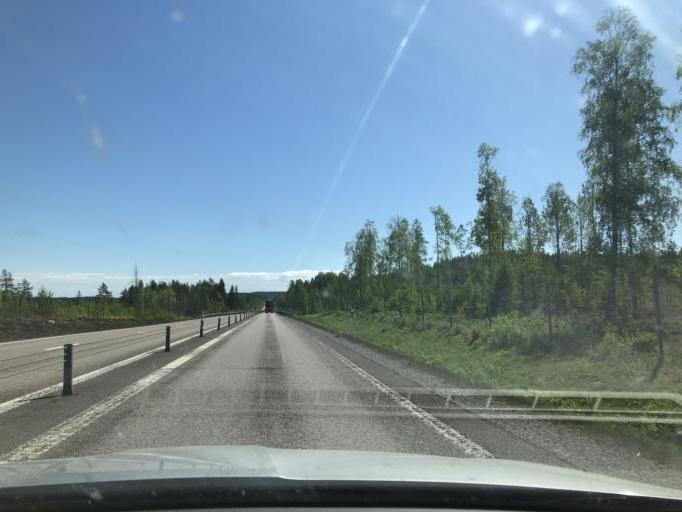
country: SE
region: Norrbotten
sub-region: Kalix Kommun
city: Toere
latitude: 65.9030
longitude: 22.8554
